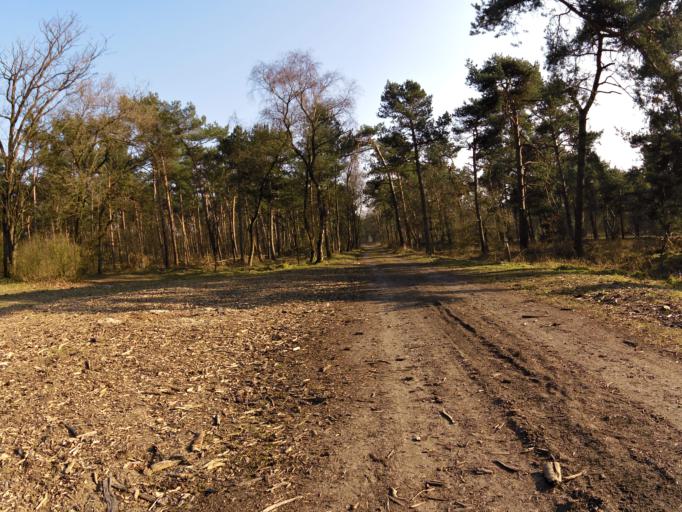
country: NL
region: North Brabant
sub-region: Gemeente Maasdonk
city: Geffen
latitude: 51.7201
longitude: 5.4108
